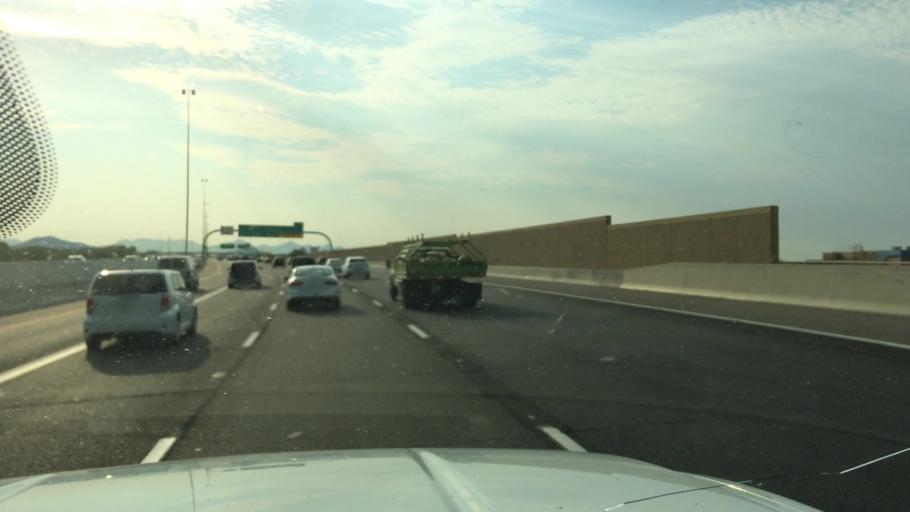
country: US
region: Arizona
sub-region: Maricopa County
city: Peoria
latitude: 33.6675
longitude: -112.1331
